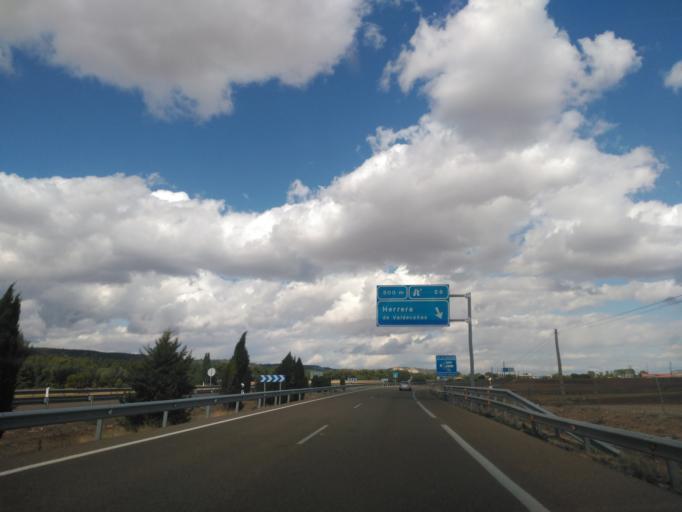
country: ES
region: Castille and Leon
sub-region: Provincia de Palencia
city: Cordovilla la Real
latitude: 42.0617
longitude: -4.2326
